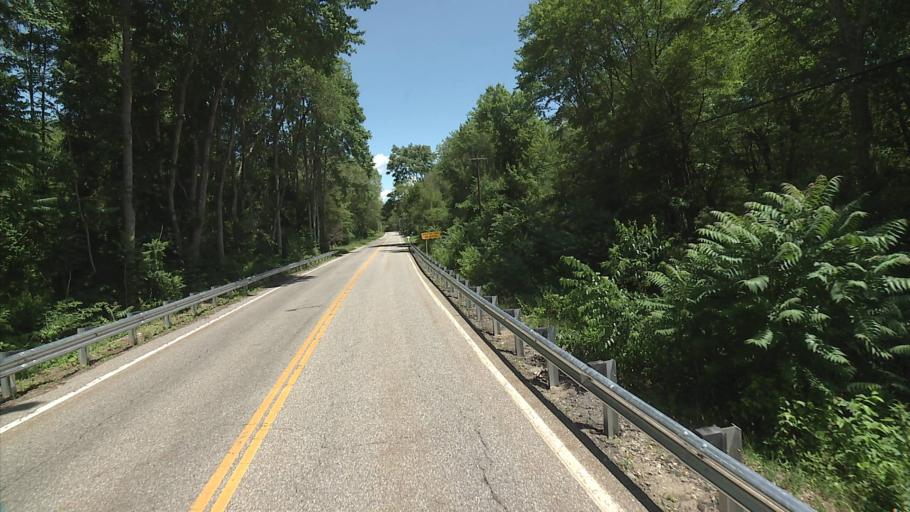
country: US
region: Connecticut
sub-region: New London County
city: Preston City
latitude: 41.5132
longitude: -71.8910
